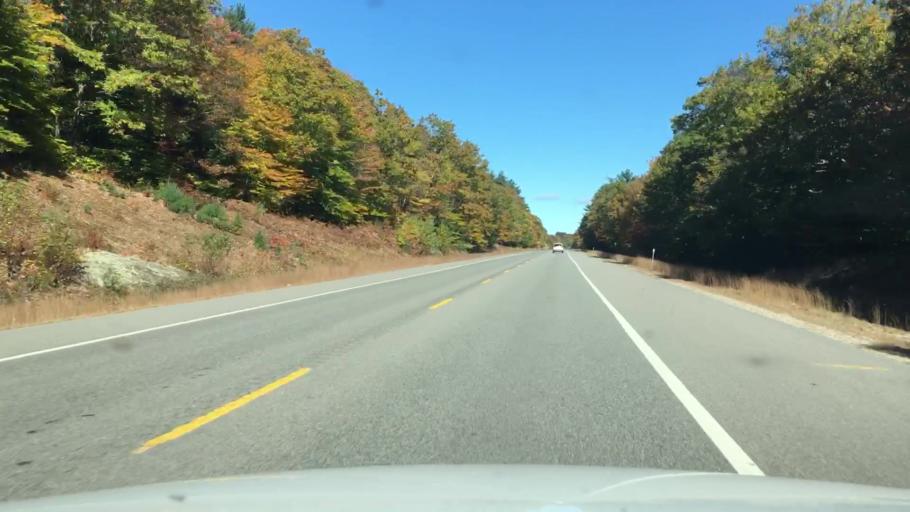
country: US
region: New Hampshire
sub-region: Carroll County
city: Sanbornville
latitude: 43.5079
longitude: -71.0290
